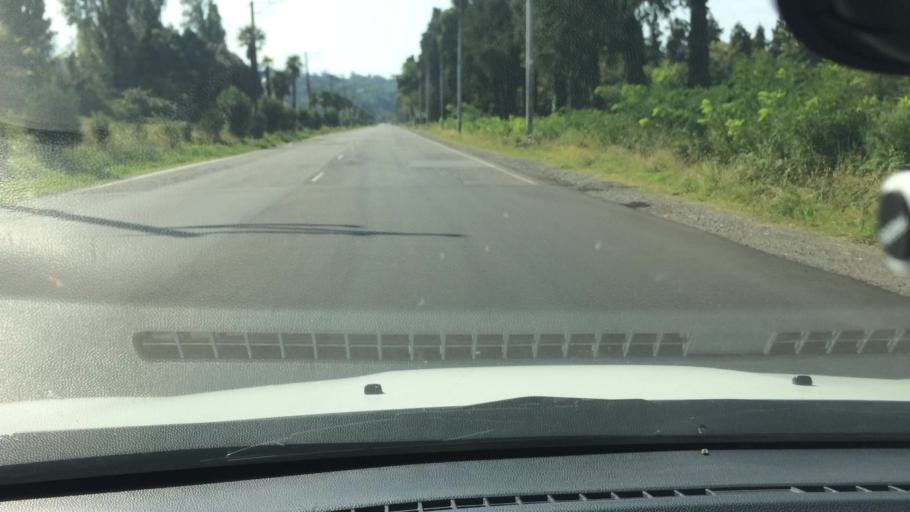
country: GE
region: Ajaria
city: Kobuleti
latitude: 41.7880
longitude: 41.7669
